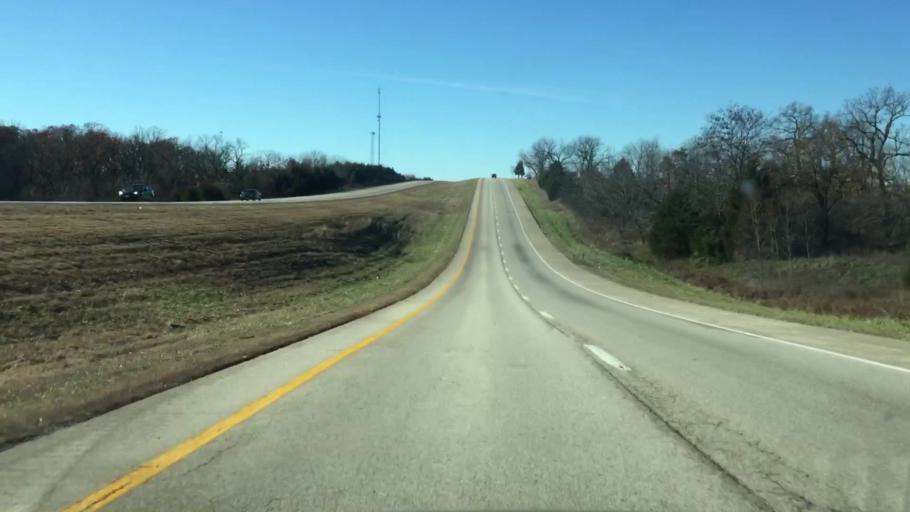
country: US
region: Missouri
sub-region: Cole County
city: Saint Martins
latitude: 38.4197
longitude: -92.3404
